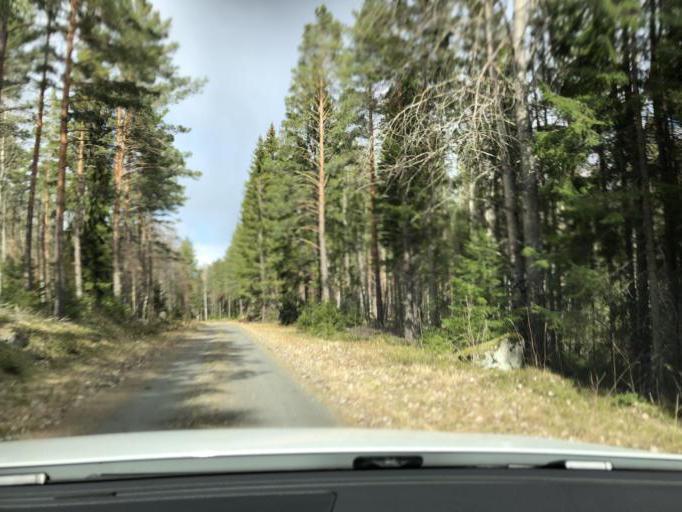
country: SE
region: Gaevleborg
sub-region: Gavle Kommun
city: Hedesunda
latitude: 60.3309
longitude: 17.1073
